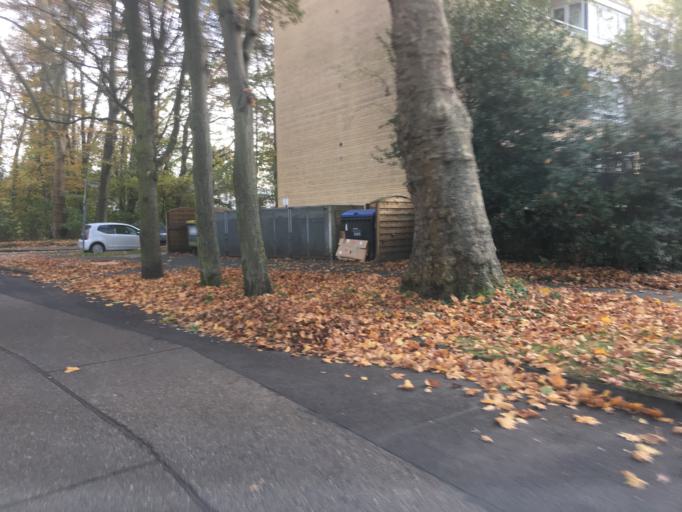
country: DE
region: North Rhine-Westphalia
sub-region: Regierungsbezirk Koln
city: Bayenthal
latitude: 50.8941
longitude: 6.9645
